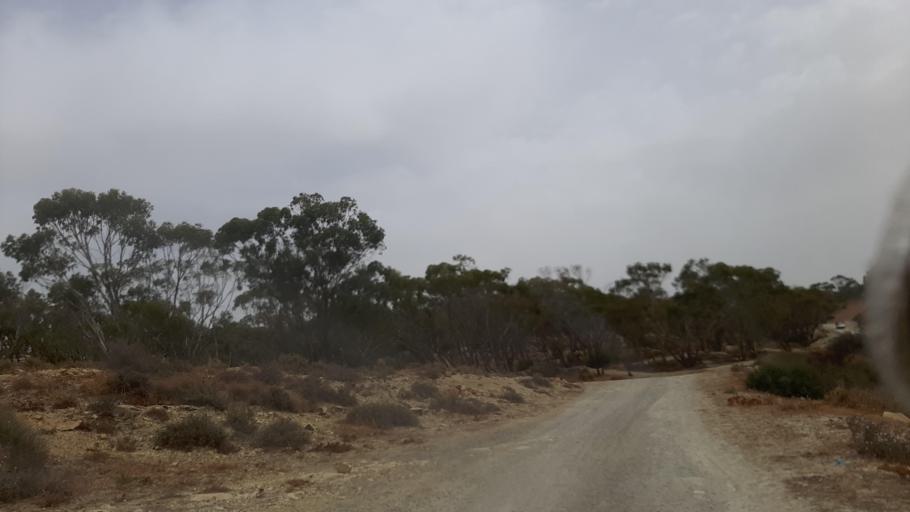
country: TN
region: Tunis
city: La Mohammedia
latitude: 36.5683
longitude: 10.1404
